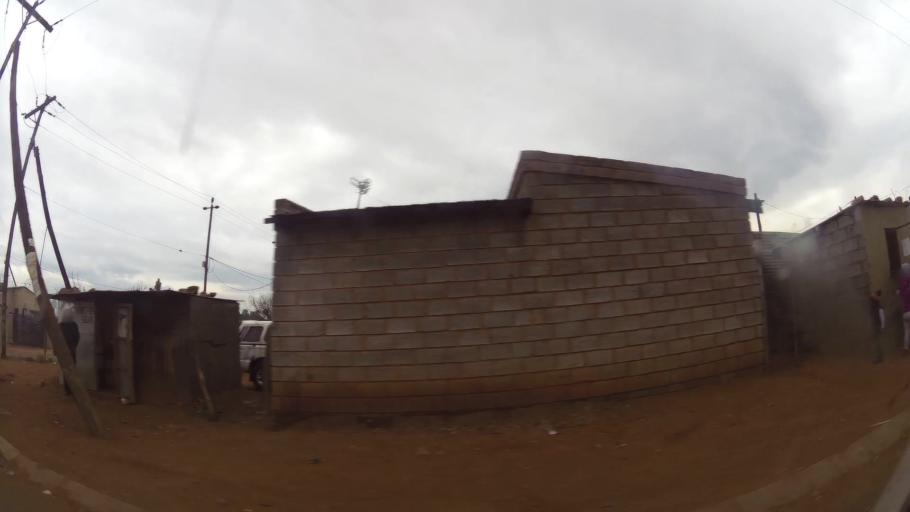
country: ZA
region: Gauteng
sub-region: Ekurhuleni Metropolitan Municipality
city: Germiston
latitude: -26.3702
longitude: 28.1693
